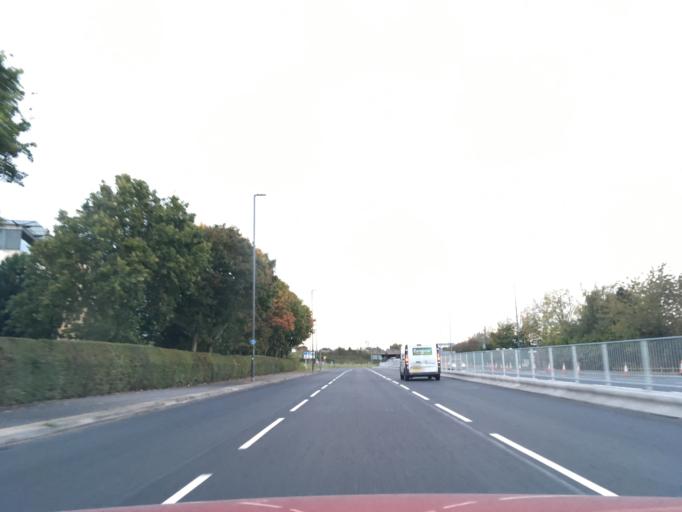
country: GB
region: England
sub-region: South Gloucestershire
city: Almondsbury
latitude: 51.5448
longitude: -2.5677
